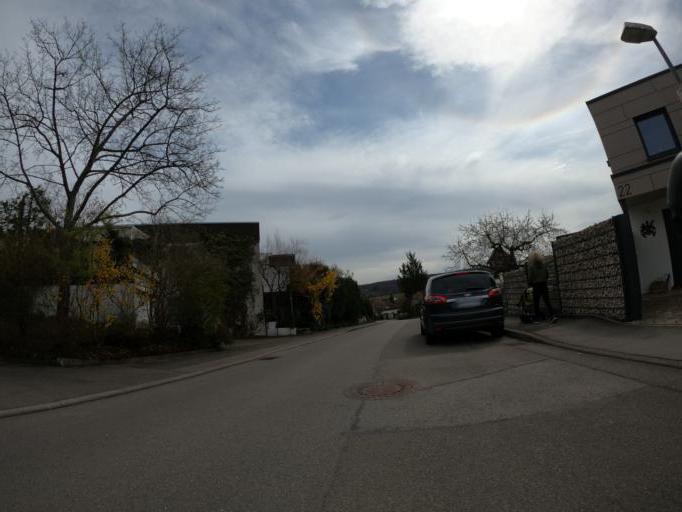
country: DE
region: Baden-Wuerttemberg
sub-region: Regierungsbezirk Stuttgart
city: Waldenbuch
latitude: 48.6396
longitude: 9.1429
